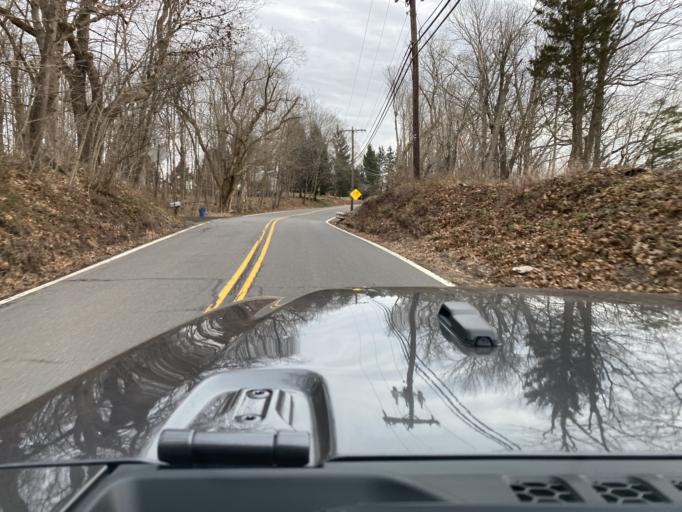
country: US
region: New Jersey
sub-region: Somerset County
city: Bloomingdale
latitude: 40.5082
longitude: -74.7256
